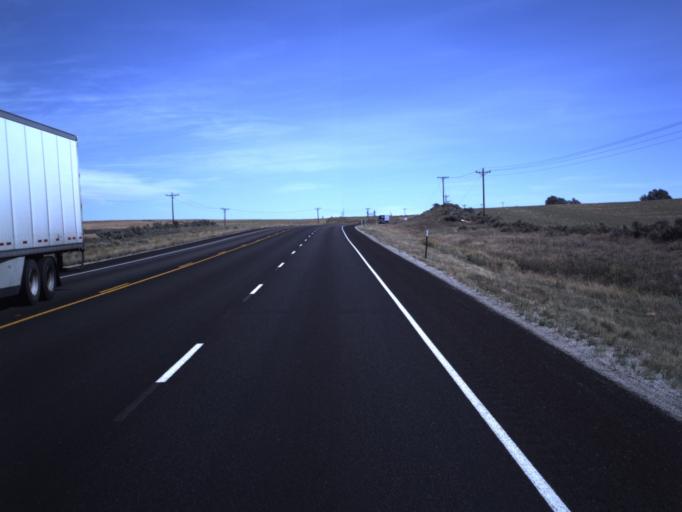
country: US
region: Utah
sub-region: San Juan County
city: Monticello
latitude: 37.8728
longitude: -109.2677
